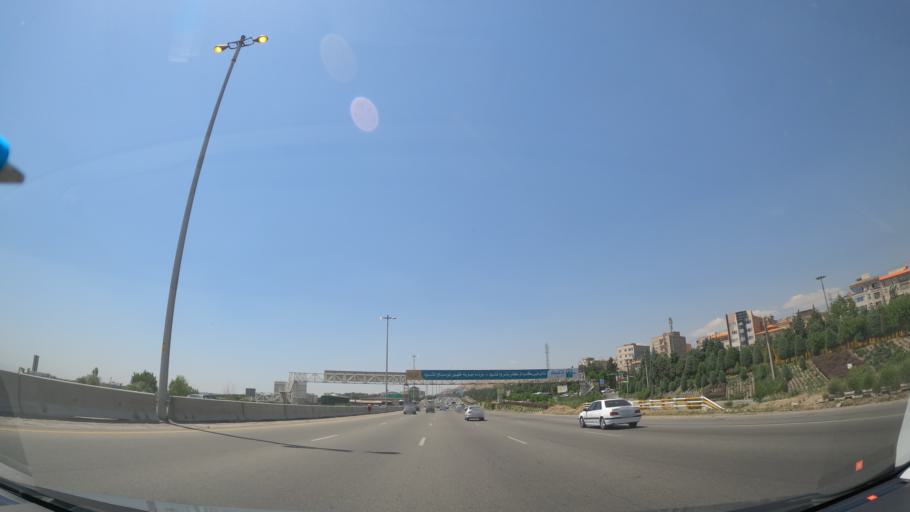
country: IR
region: Alborz
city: Karaj
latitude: 35.7749
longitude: 51.0398
